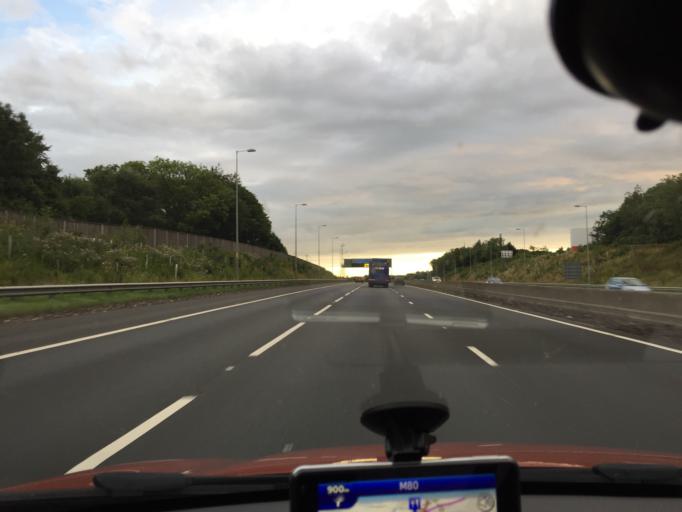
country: GB
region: Scotland
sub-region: North Lanarkshire
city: Glenboig
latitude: 55.9298
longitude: -4.0400
